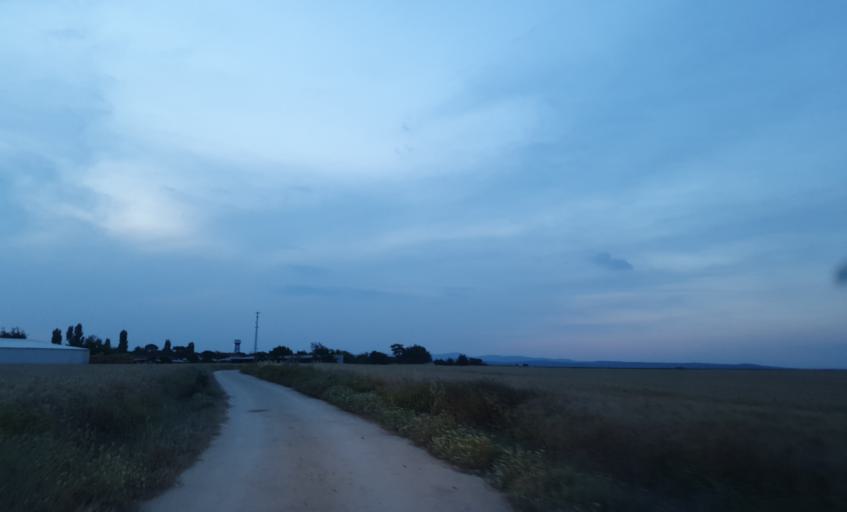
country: TR
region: Kirklareli
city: Vize
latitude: 41.5140
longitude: 27.7455
